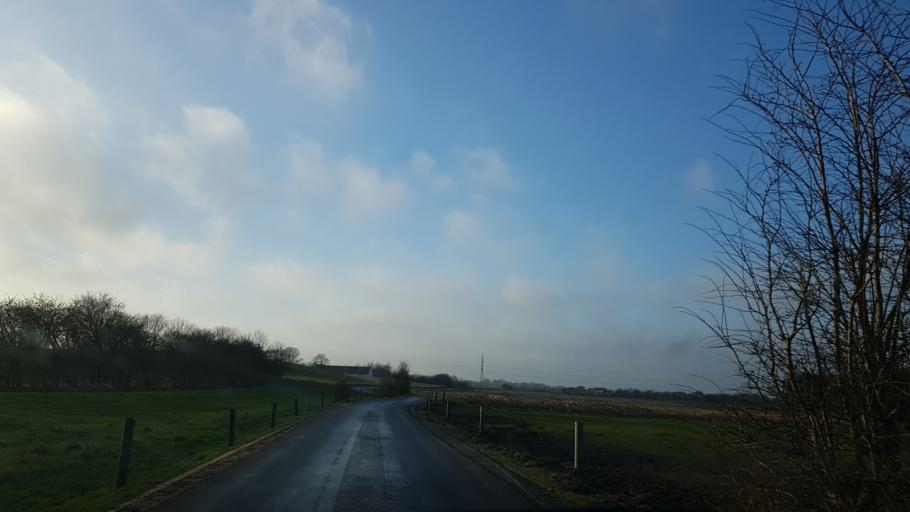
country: DK
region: South Denmark
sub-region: Aabenraa Kommune
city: Rodekro
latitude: 55.1553
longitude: 9.3056
